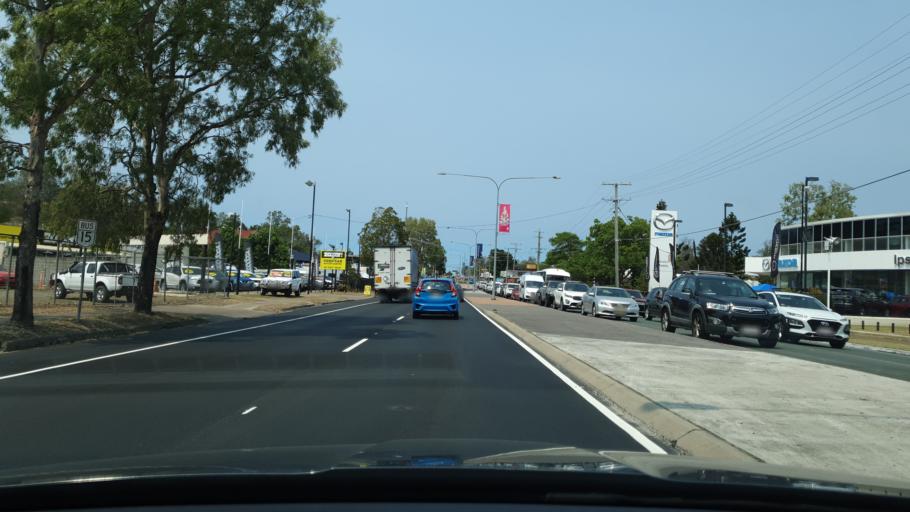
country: AU
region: Queensland
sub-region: Ipswich
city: Bundamba
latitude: -27.6097
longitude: 152.8080
